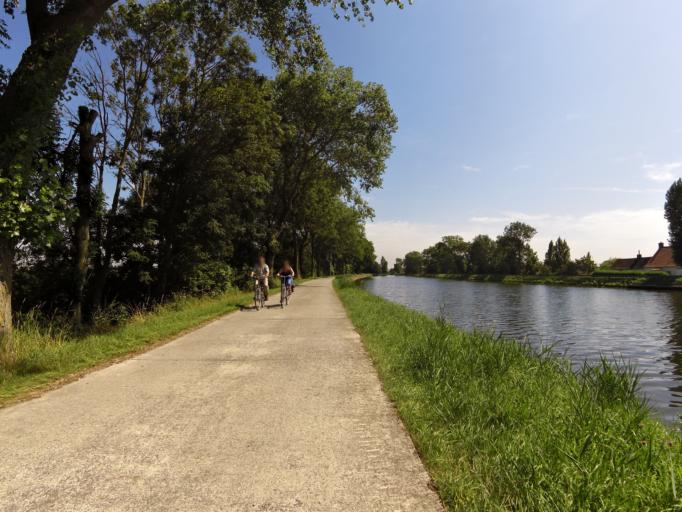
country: BE
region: Flanders
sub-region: Provincie West-Vlaanderen
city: Oudenburg
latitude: 51.2028
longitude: 3.0329
